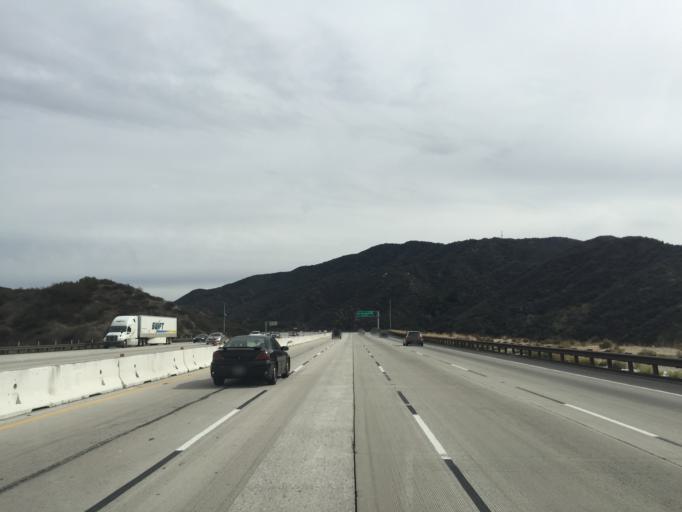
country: US
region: California
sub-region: Los Angeles County
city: Burbank
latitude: 34.2379
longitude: -118.3053
